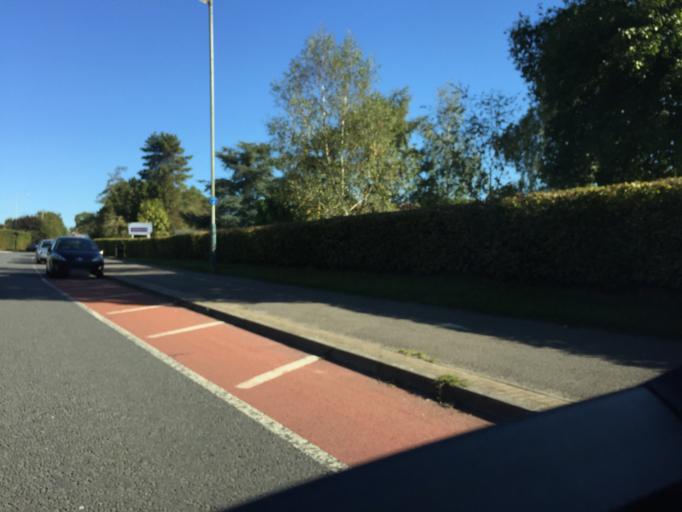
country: GB
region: England
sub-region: Wiltshire
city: Chippenham
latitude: 51.4677
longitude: -2.1349
